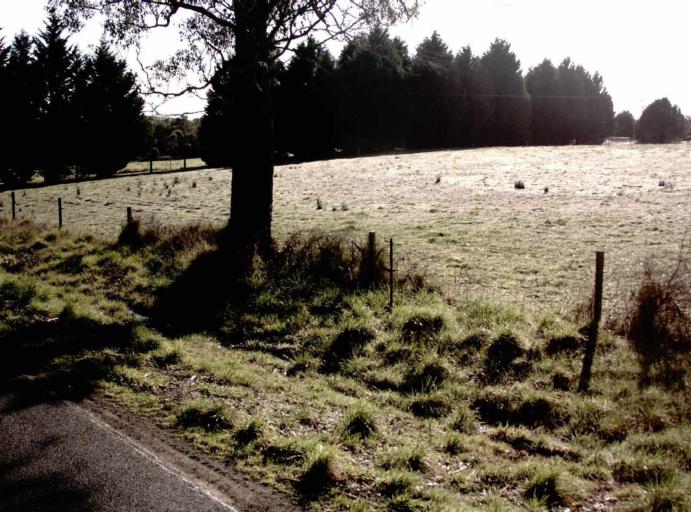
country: AU
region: Tasmania
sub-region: Dorset
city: Bridport
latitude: -41.1032
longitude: 147.1978
